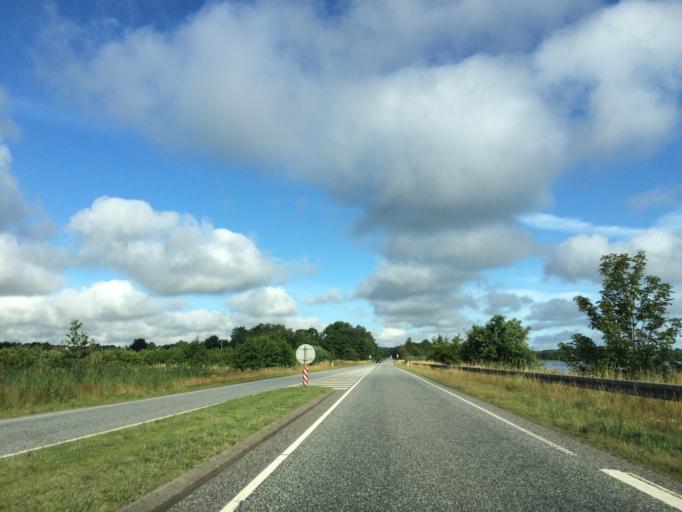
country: DK
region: Central Jutland
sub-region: Viborg Kommune
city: Bjerringbro
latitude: 56.3062
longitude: 9.6063
